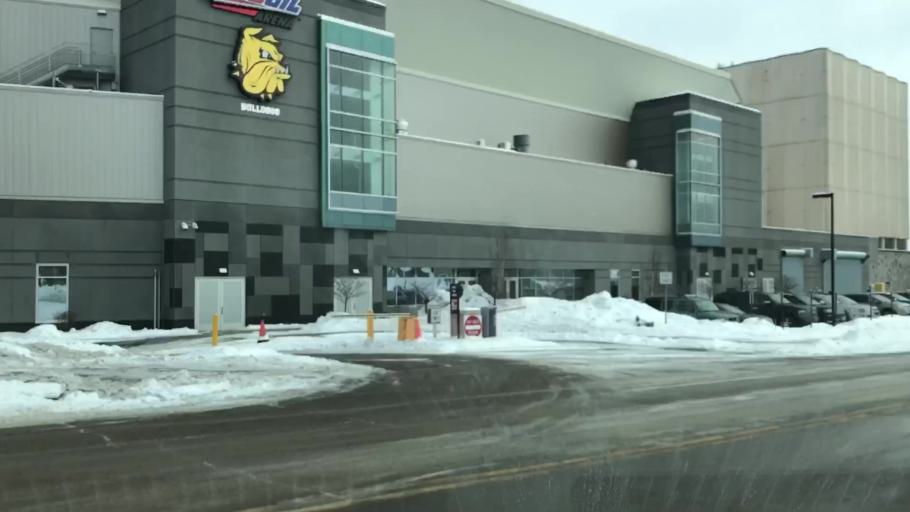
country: US
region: Minnesota
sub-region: Saint Louis County
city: Duluth
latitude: 46.7802
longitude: -92.1008
